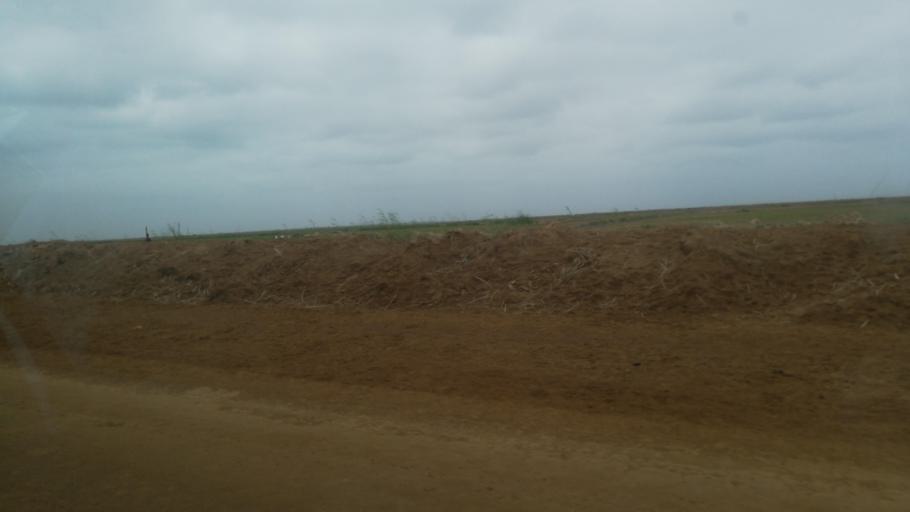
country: SN
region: Saint-Louis
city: Saint-Louis
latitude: 16.3183
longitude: -16.2358
